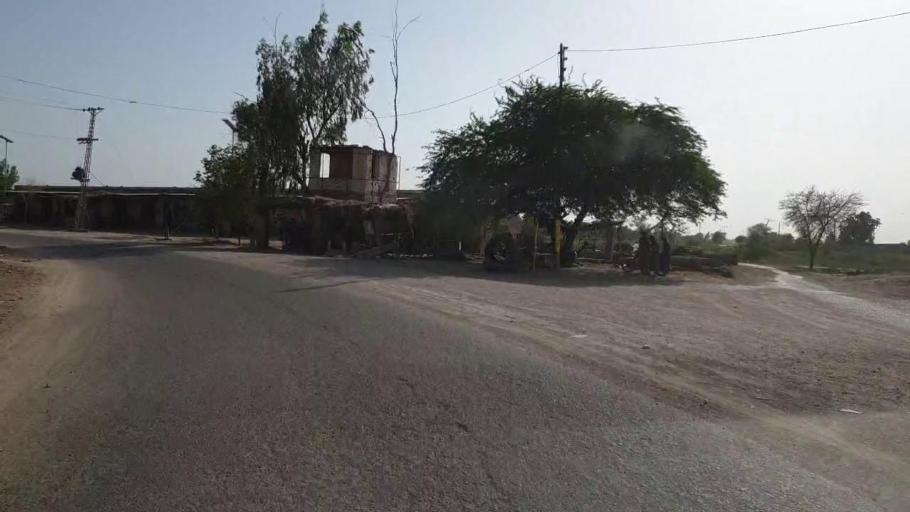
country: PK
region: Sindh
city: Daur
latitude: 26.4736
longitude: 68.4543
